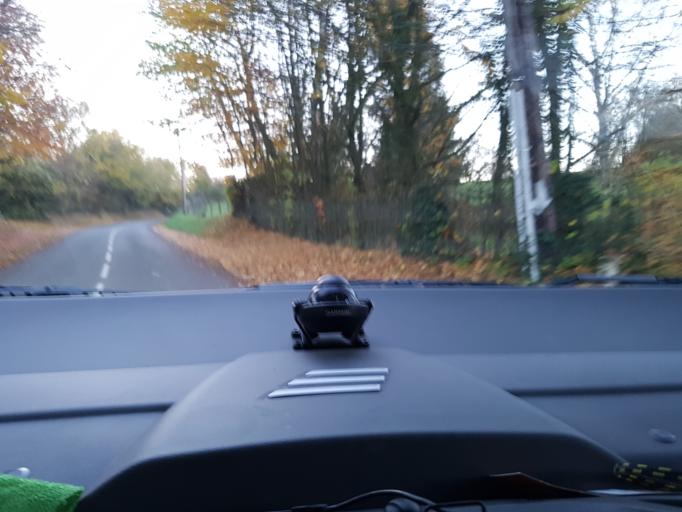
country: FR
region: Nord-Pas-de-Calais
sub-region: Departement du Pas-de-Calais
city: Campagne-les-Hesdin
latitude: 50.3402
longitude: 1.8327
